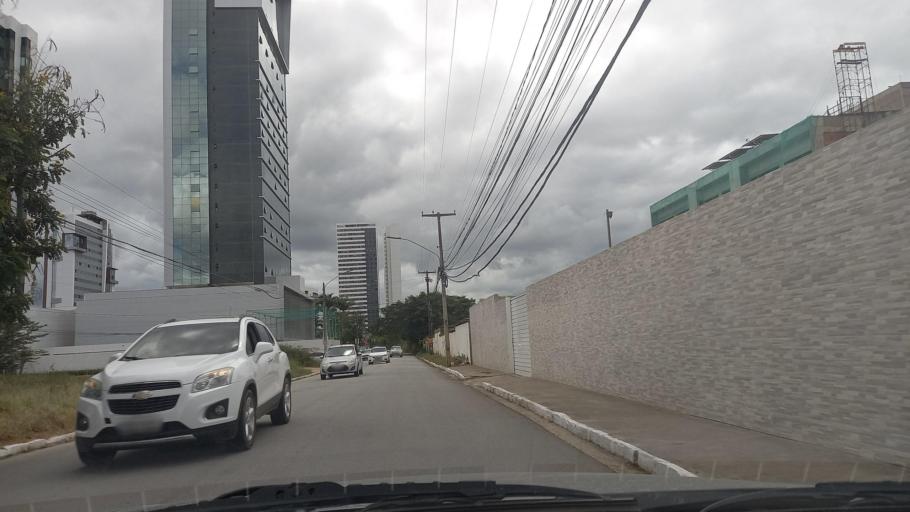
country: BR
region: Pernambuco
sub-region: Caruaru
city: Caruaru
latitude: -8.2621
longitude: -35.9658
